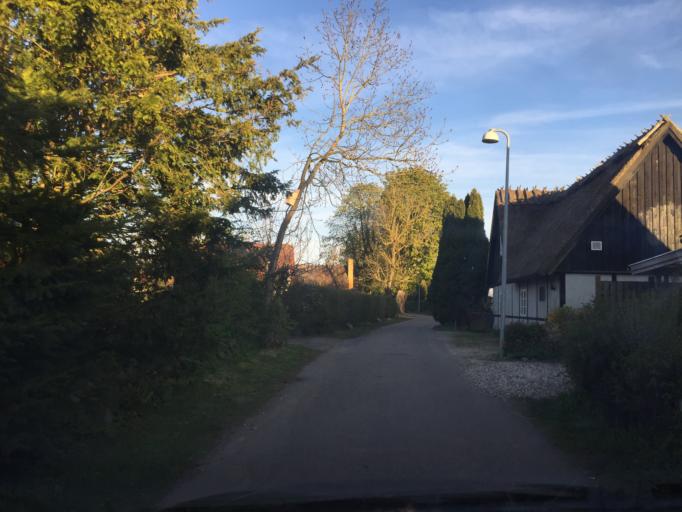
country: DK
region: Capital Region
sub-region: Hoje-Taastrup Kommune
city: Taastrup
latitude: 55.6846
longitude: 12.2924
